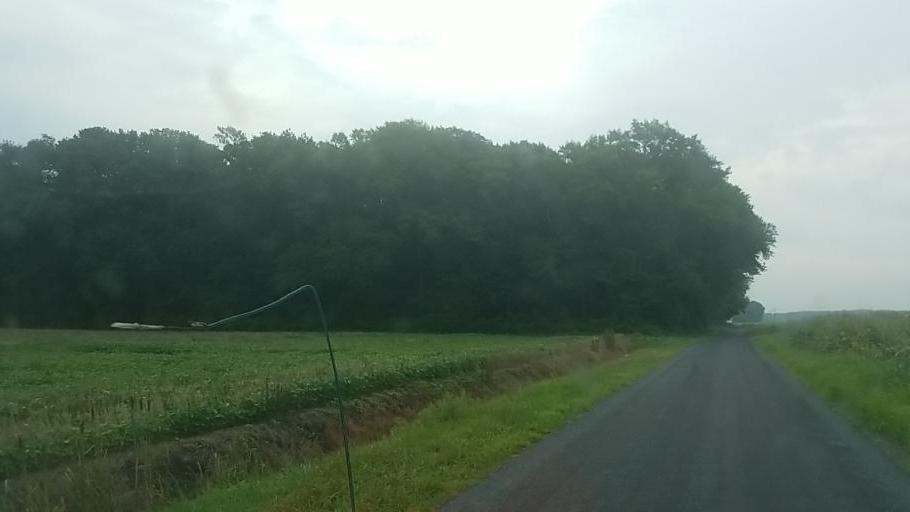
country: US
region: Delaware
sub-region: Sussex County
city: Selbyville
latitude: 38.4449
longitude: -75.2719
